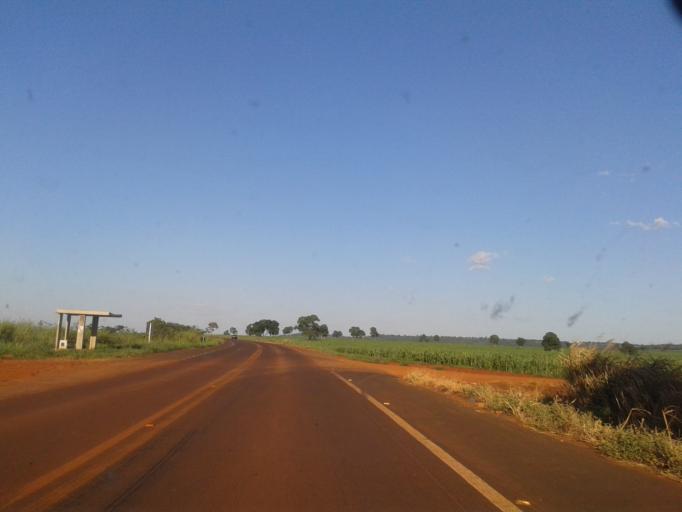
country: BR
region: Minas Gerais
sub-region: Capinopolis
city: Capinopolis
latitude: -18.7120
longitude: -49.8432
